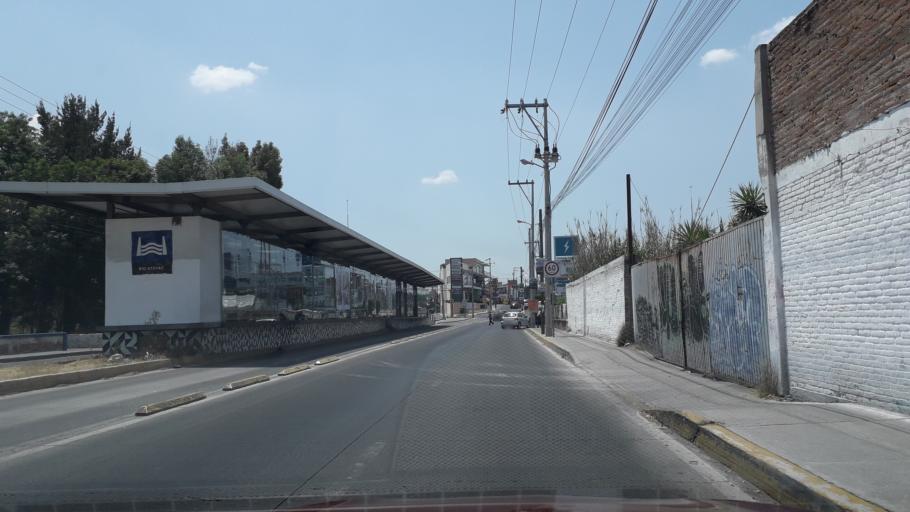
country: MX
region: Puebla
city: Puebla
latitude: 19.0225
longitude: -98.2254
